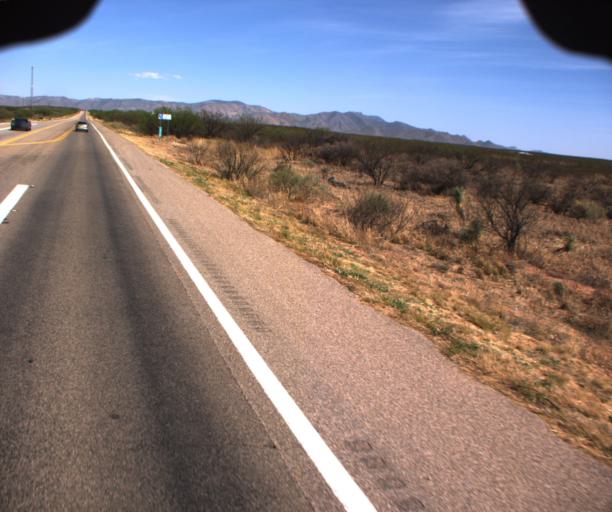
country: US
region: Arizona
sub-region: Cochise County
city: Sierra Vista Southeast
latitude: 31.5515
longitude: -110.1173
